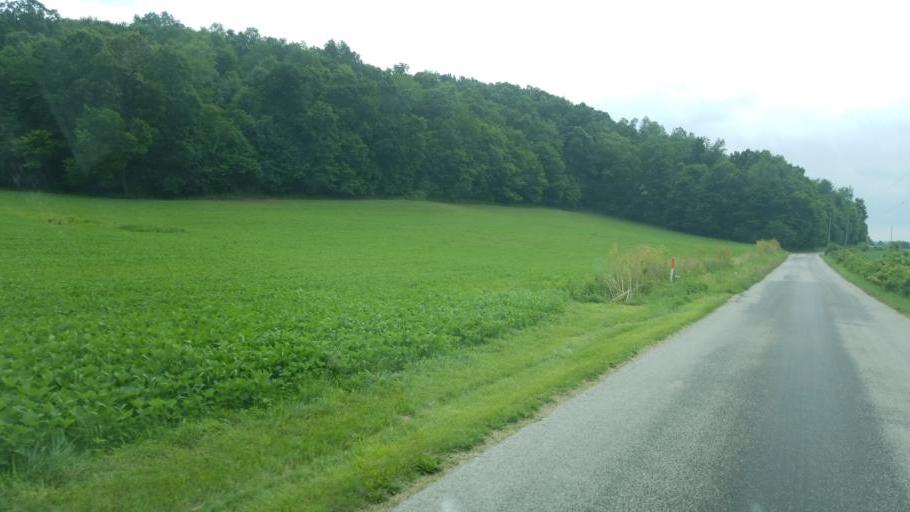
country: US
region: Ohio
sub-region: Licking County
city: Utica
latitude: 40.1702
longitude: -82.4300
